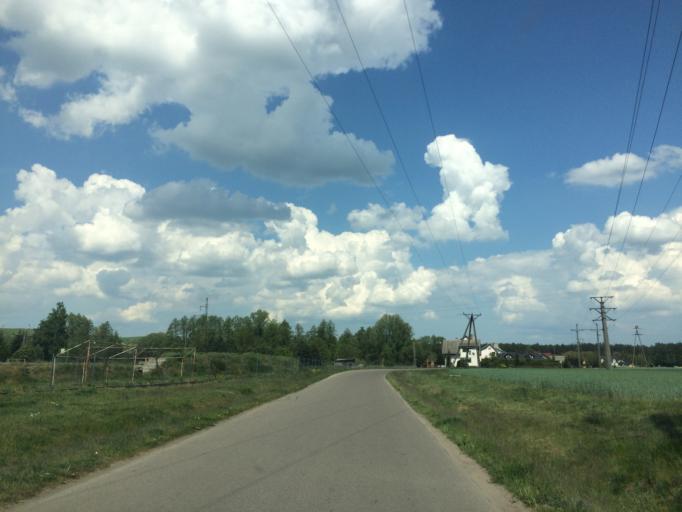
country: PL
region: Warmian-Masurian Voivodeship
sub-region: Powiat nowomiejski
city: Nowe Miasto Lubawskie
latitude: 53.4434
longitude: 19.6083
